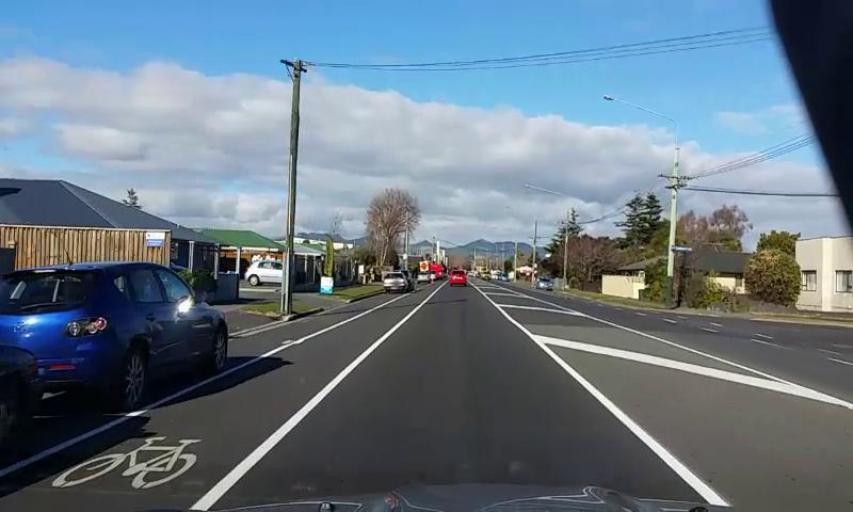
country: NZ
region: Canterbury
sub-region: Christchurch City
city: Christchurch
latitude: -43.5024
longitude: 172.6623
